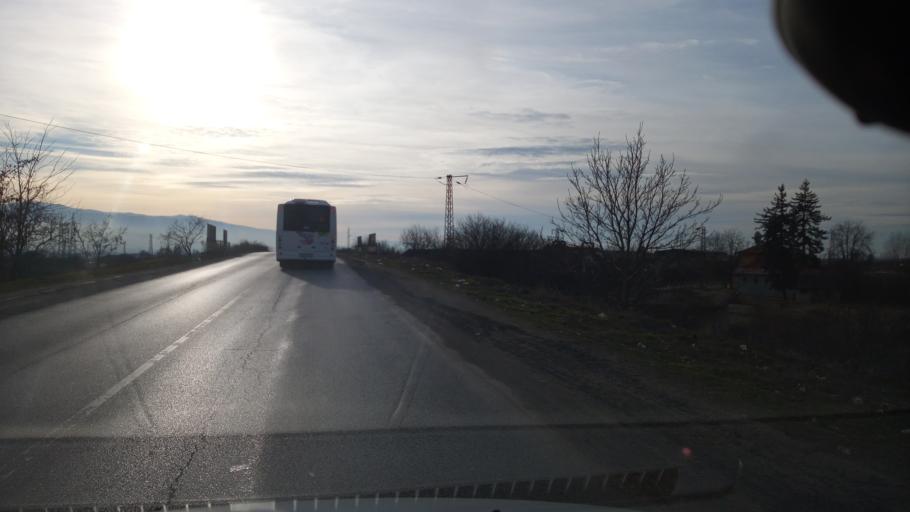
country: BG
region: Sofia-Capital
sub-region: Stolichna Obshtina
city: Bukhovo
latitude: 42.7259
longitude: 23.5531
